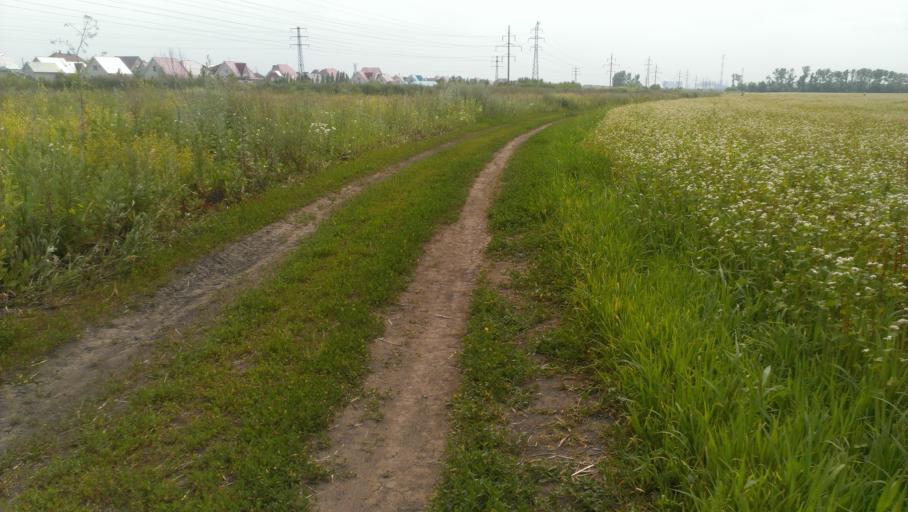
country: RU
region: Altai Krai
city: Novosilikatnyy
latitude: 53.3730
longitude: 83.6489
